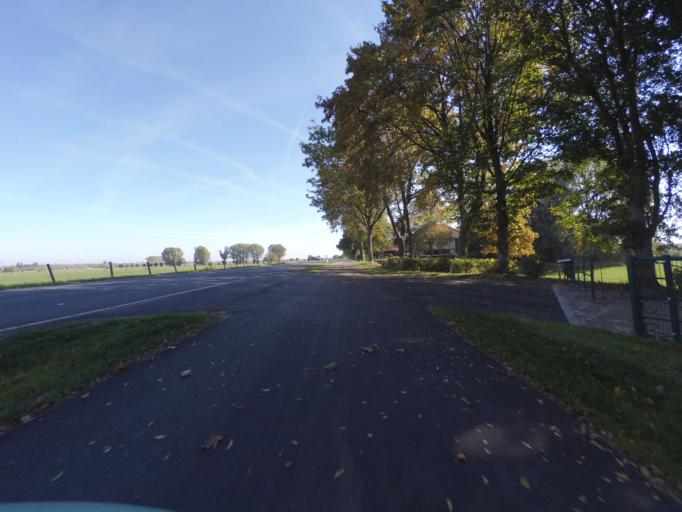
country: DE
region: North Rhine-Westphalia
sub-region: Regierungsbezirk Dusseldorf
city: Emmerich
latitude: 51.8206
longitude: 6.2322
